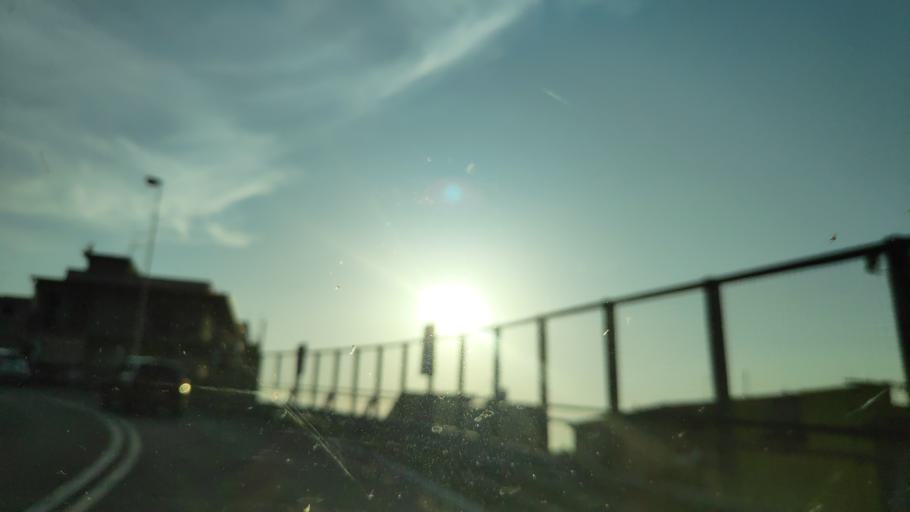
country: IT
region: Calabria
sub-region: Provincia di Reggio Calabria
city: Scilla
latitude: 38.2521
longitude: 15.7211
